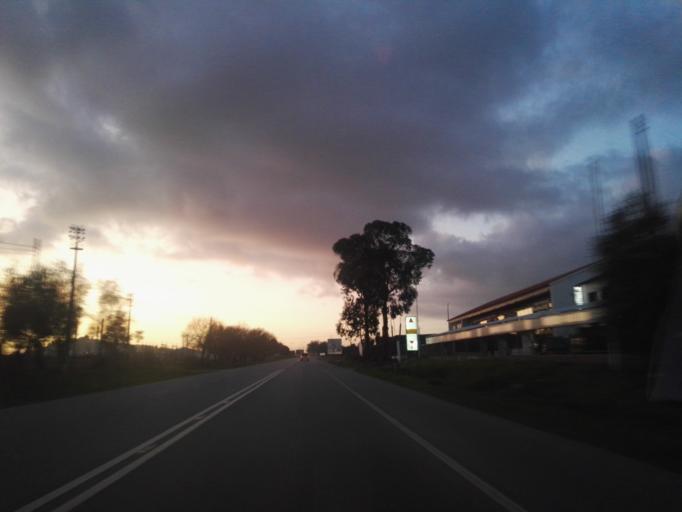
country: PT
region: Evora
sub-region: Montemor-O-Novo
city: Montemor-o-Novo
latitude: 38.6451
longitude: -8.1966
